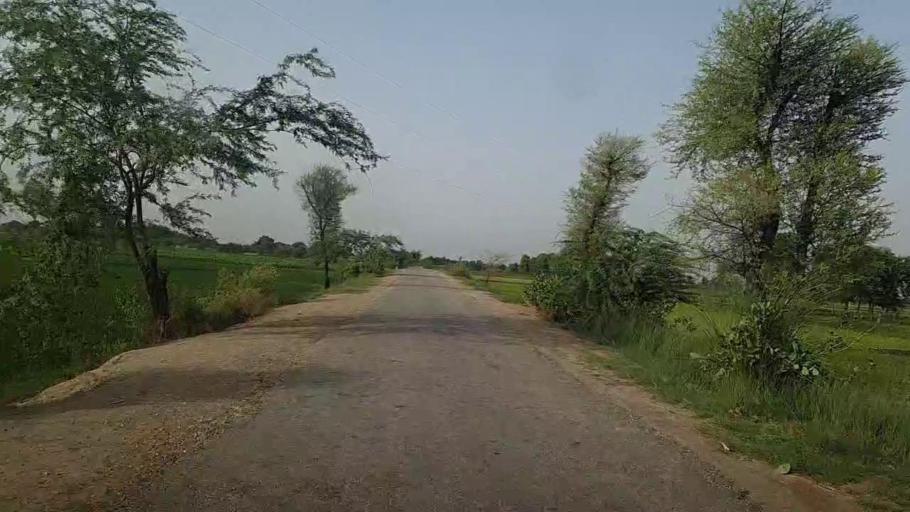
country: PK
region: Sindh
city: Mehar
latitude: 27.1377
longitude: 67.7904
